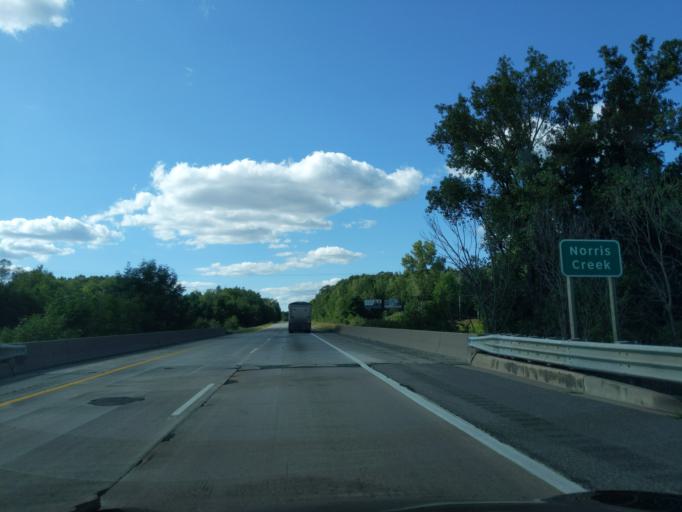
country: US
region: Michigan
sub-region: Muskegon County
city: Fruitport
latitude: 43.1278
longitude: -86.1398
